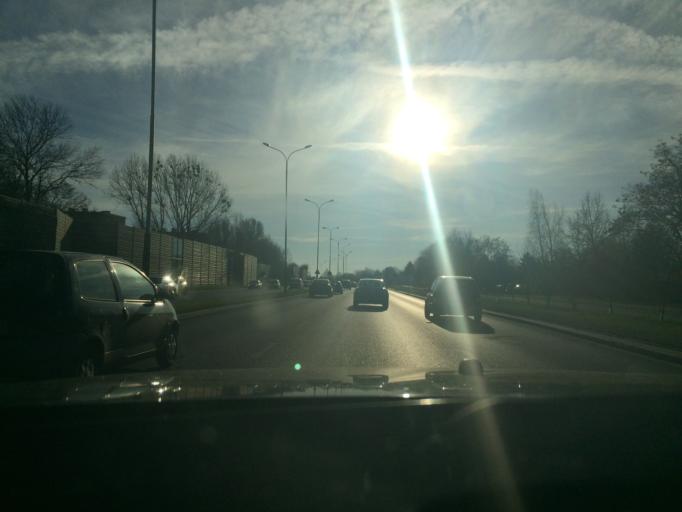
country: PL
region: Lodz Voivodeship
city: Lodz
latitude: 51.7342
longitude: 19.4420
